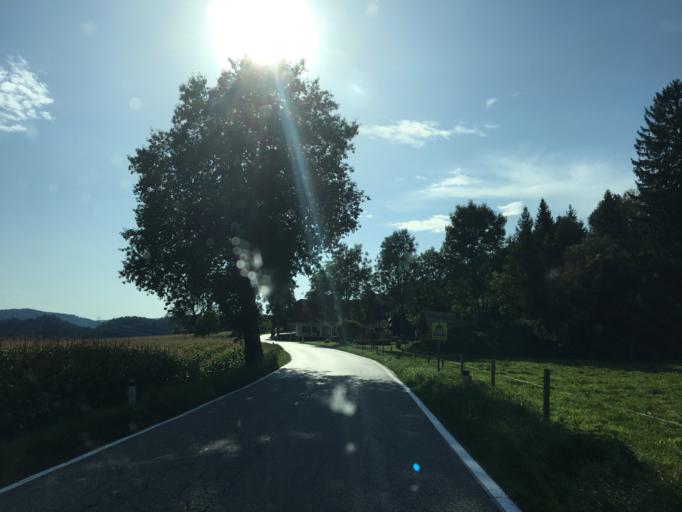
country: AT
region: Carinthia
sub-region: Politischer Bezirk Volkermarkt
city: Voelkermarkt
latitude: 46.6930
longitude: 14.6460
